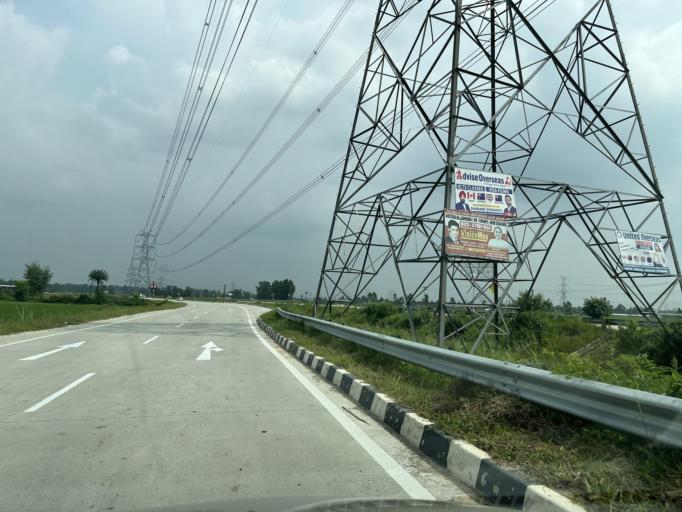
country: IN
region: Uttarakhand
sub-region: Udham Singh Nagar
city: Jaspur
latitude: 29.2842
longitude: 78.8584
